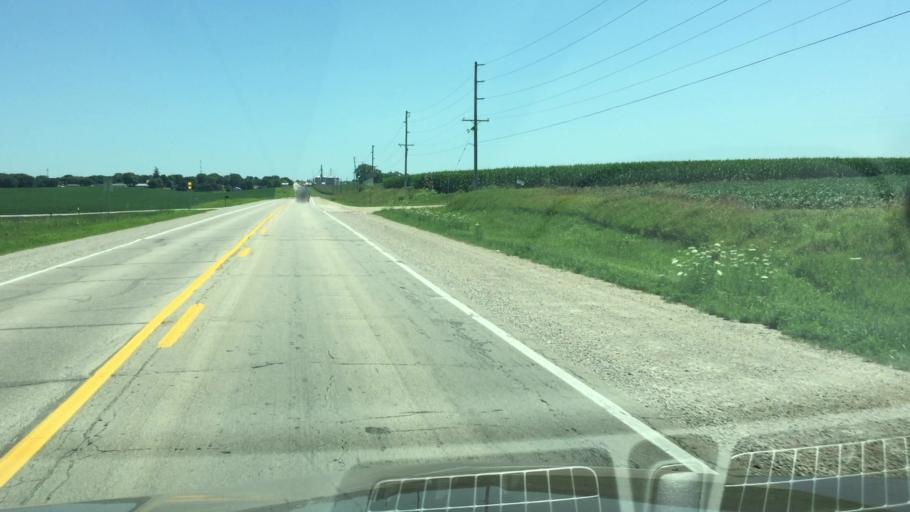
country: US
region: Iowa
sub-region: Cedar County
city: Mechanicsville
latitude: 41.8885
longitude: -91.1728
